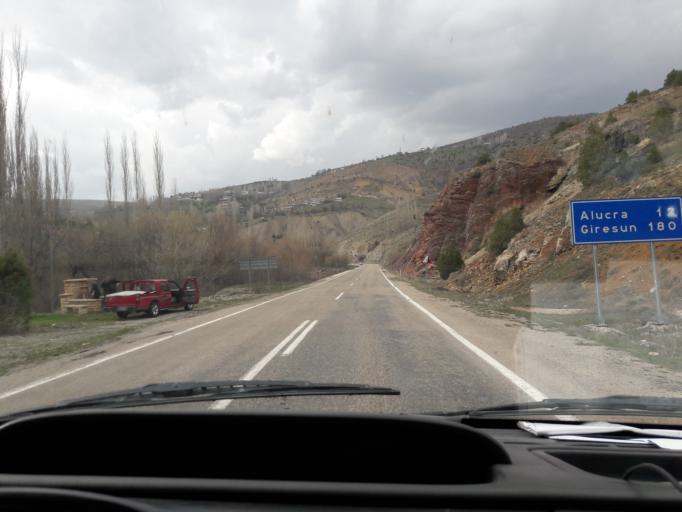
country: TR
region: Giresun
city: Alucra
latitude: 40.2678
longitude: 38.8843
